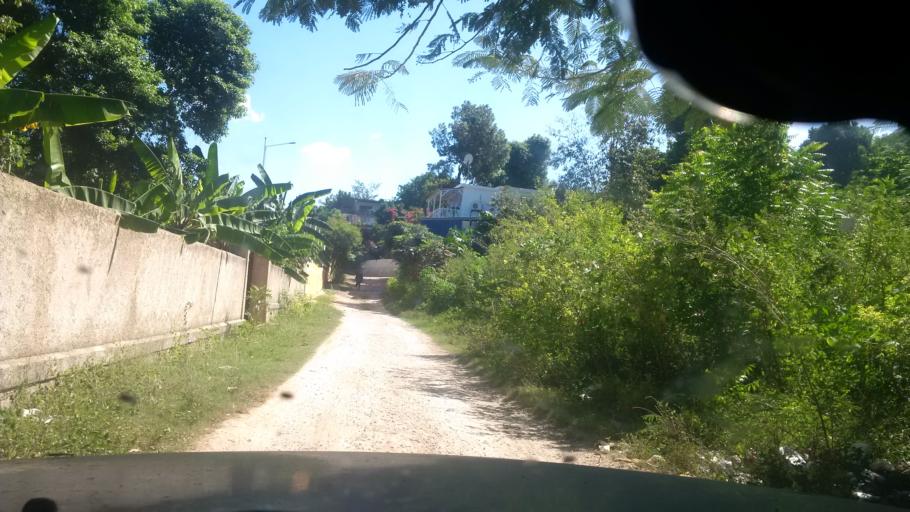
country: HT
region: Ouest
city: Grangwav
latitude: 18.4300
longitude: -72.7941
